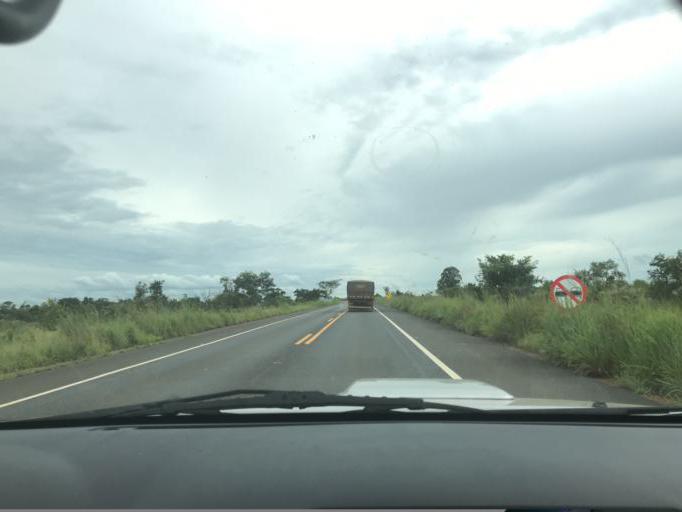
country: BR
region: Minas Gerais
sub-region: Araxa
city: Araxa
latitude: -19.3810
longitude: -46.8594
